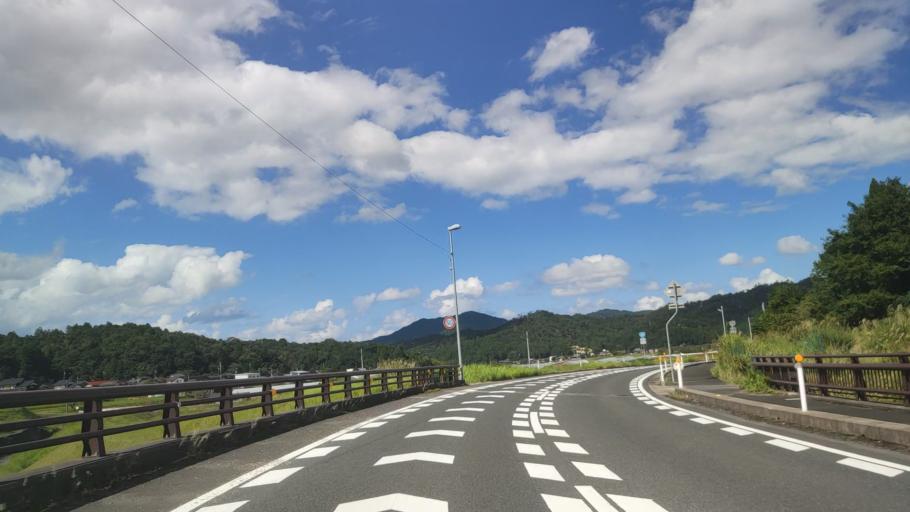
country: JP
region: Hyogo
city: Toyooka
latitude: 35.5663
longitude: 134.9737
